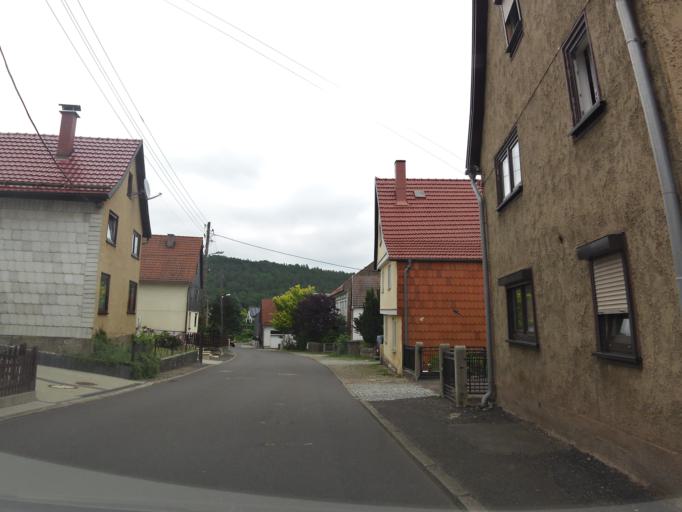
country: DE
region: Thuringia
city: Tabarz
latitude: 50.8846
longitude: 10.4783
